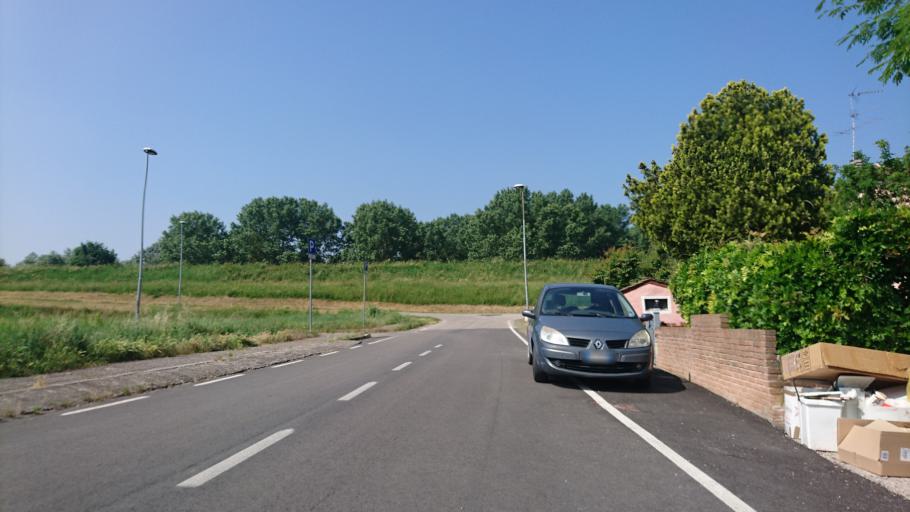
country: IT
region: Lombardy
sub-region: Provincia di Mantova
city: Ostiglia
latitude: 45.0713
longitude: 11.1277
